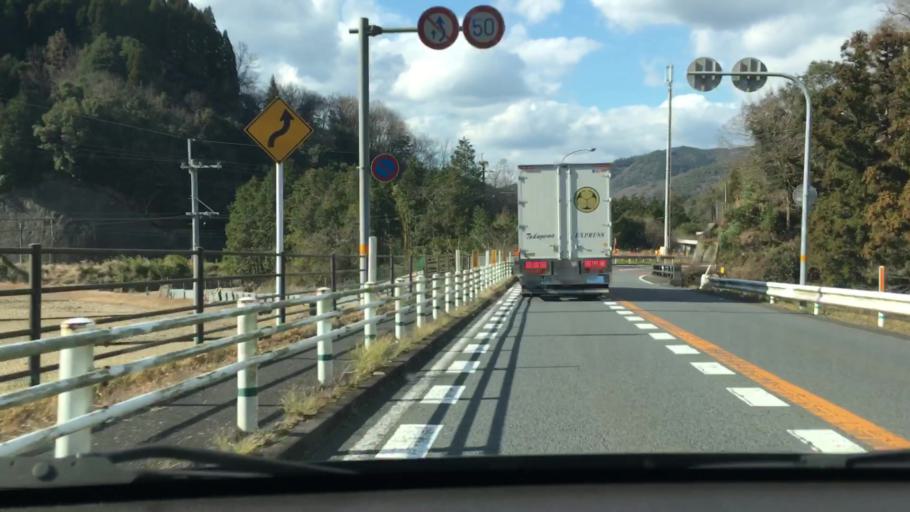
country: JP
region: Oita
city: Usuki
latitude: 32.9981
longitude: 131.7526
